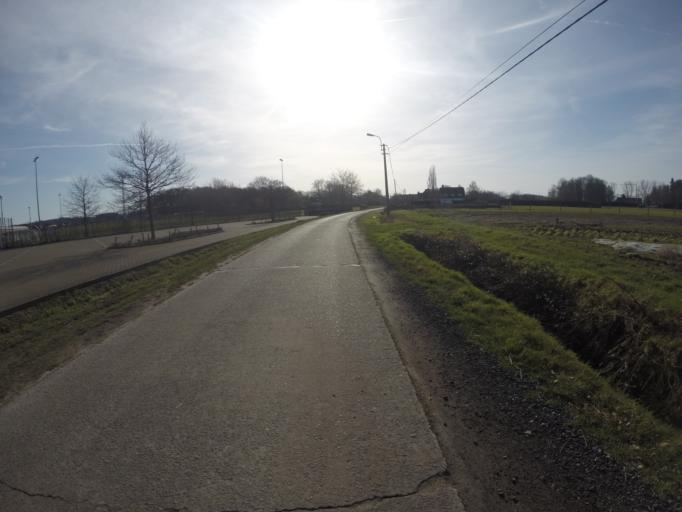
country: BE
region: Flanders
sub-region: Provincie West-Vlaanderen
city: Oostkamp
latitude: 51.1106
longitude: 3.2603
